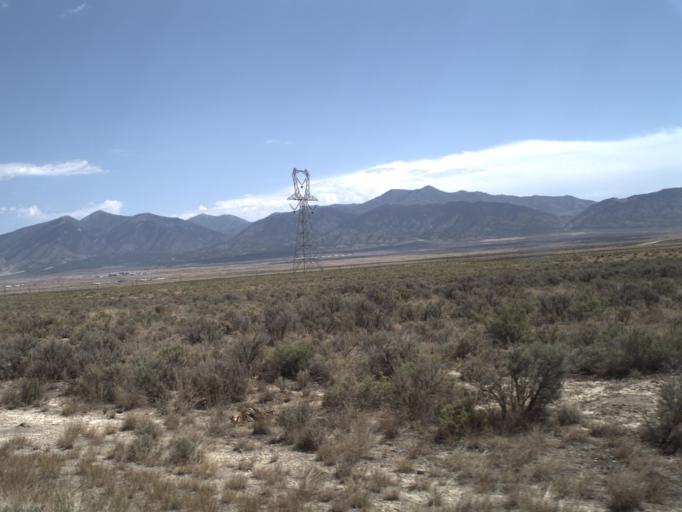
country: US
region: Utah
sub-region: Tooele County
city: Tooele
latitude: 40.2518
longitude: -112.3992
